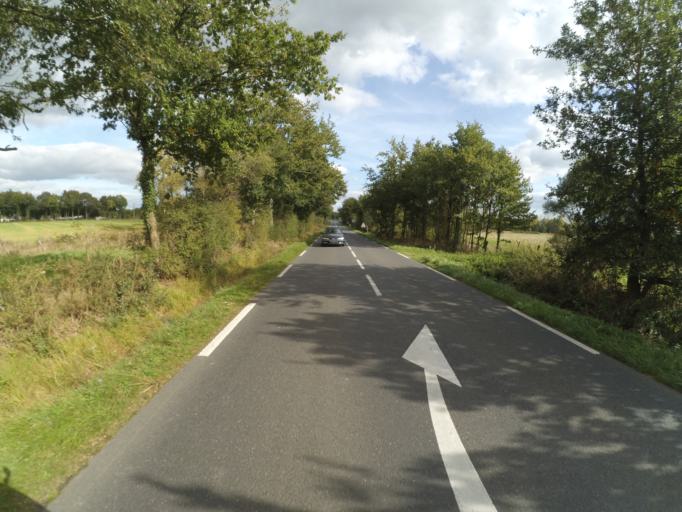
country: FR
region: Pays de la Loire
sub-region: Departement de la Loire-Atlantique
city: Notre-Dame-des-Landes
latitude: 47.4077
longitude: -1.7366
